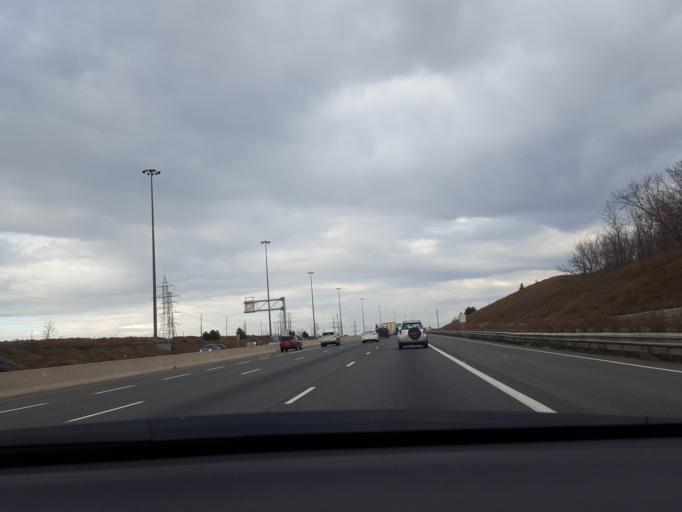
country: CA
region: Ontario
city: Mississauga
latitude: 43.5728
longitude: -79.6731
